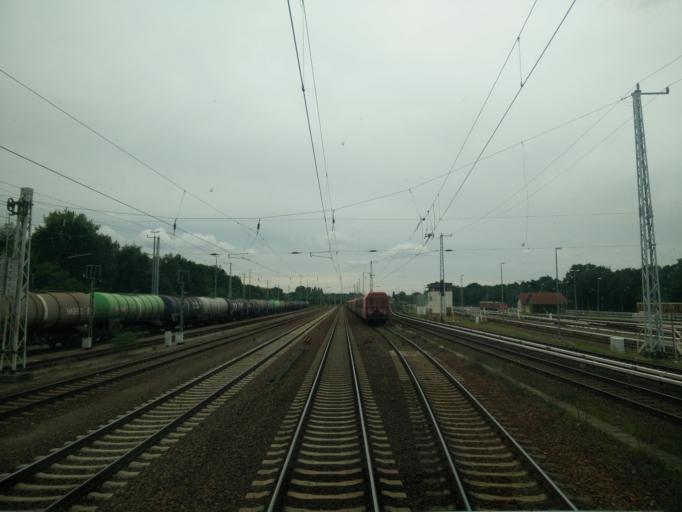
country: DE
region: Berlin
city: Grunau
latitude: 52.4060
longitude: 13.5835
